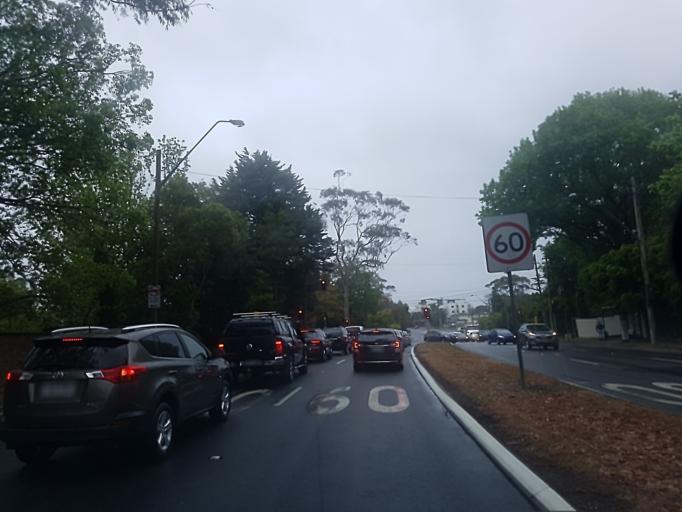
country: AU
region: New South Wales
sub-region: City of Sydney
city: Pymble
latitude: -33.7338
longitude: 151.1543
